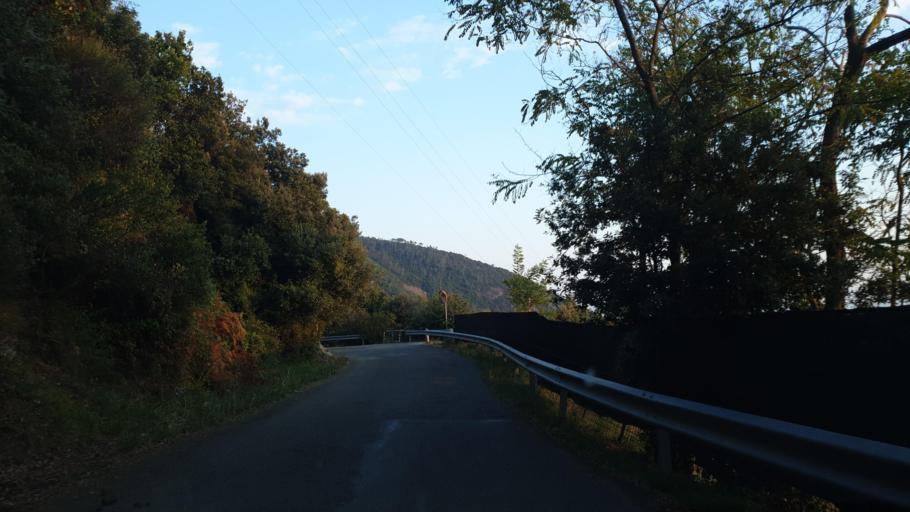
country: IT
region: Liguria
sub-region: Provincia di La Spezia
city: Bonassola
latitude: 44.1921
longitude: 9.5893
